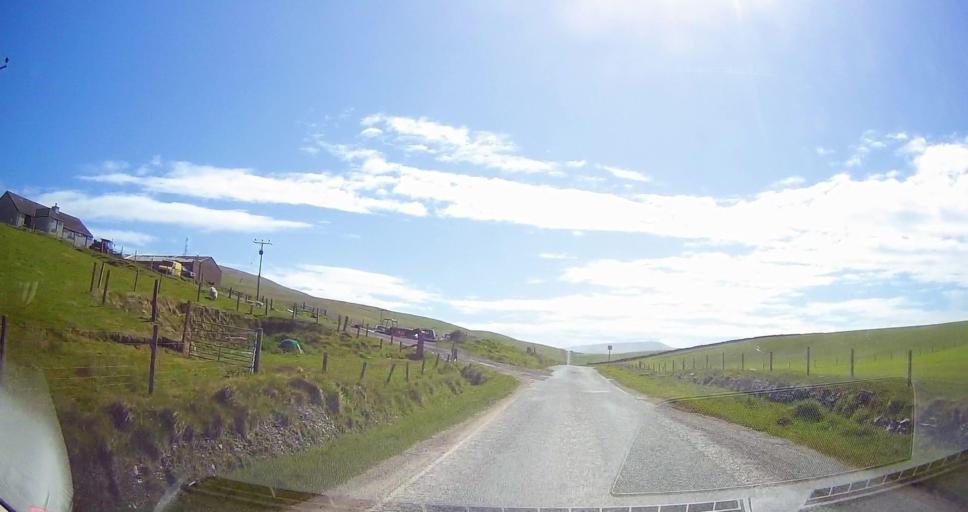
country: GB
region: Scotland
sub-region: Shetland Islands
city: Sandwick
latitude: 59.9698
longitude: -1.3176
